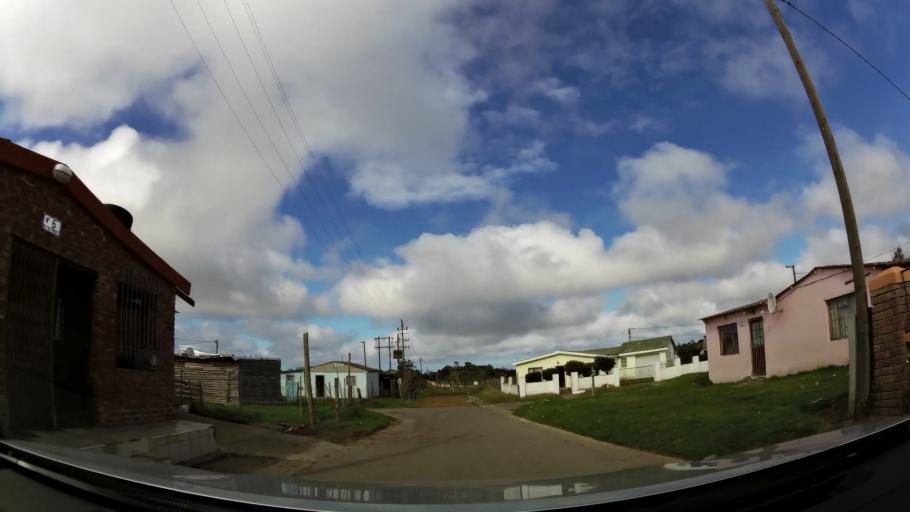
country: ZA
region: Western Cape
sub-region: Eden District Municipality
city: Plettenberg Bay
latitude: -34.0481
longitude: 23.3270
